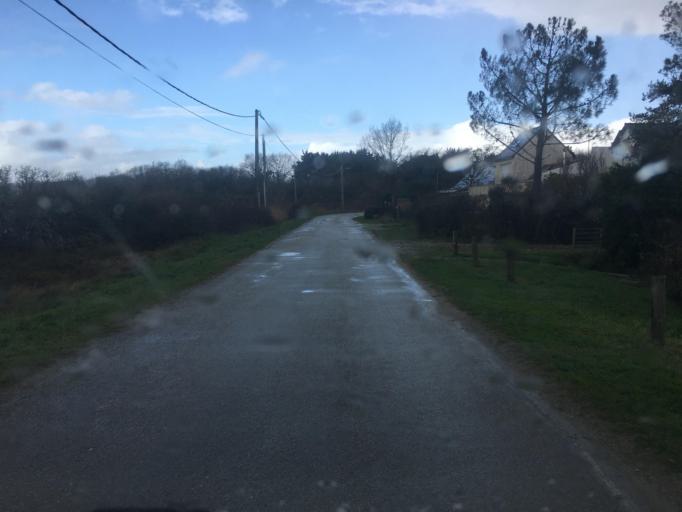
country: FR
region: Brittany
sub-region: Departement du Morbihan
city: Surzur
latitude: 47.5149
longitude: -2.6684
